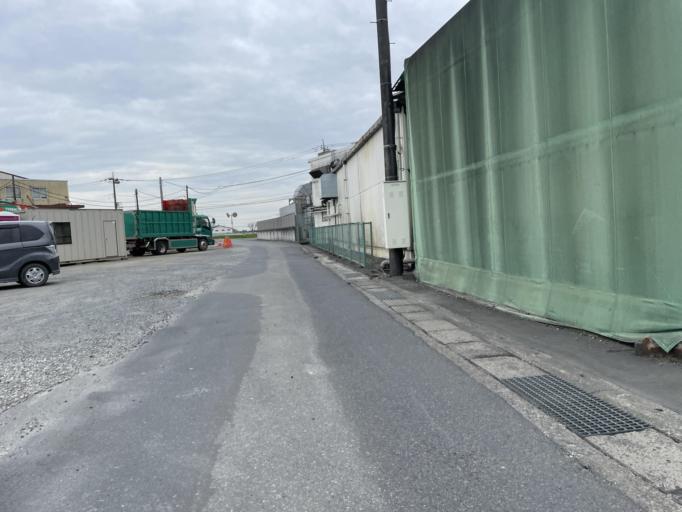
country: JP
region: Saitama
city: Shiraoka
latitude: 36.0343
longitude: 139.6512
